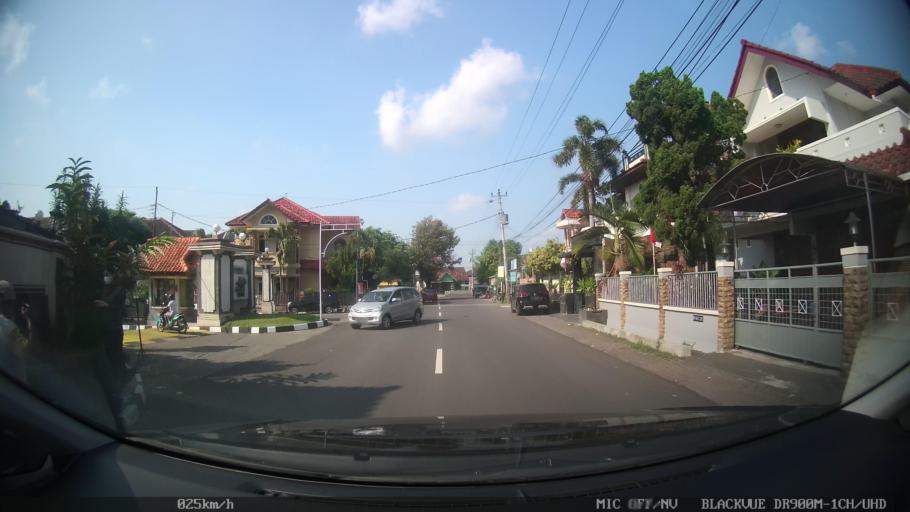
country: ID
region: Daerah Istimewa Yogyakarta
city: Depok
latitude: -7.7645
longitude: 110.3979
